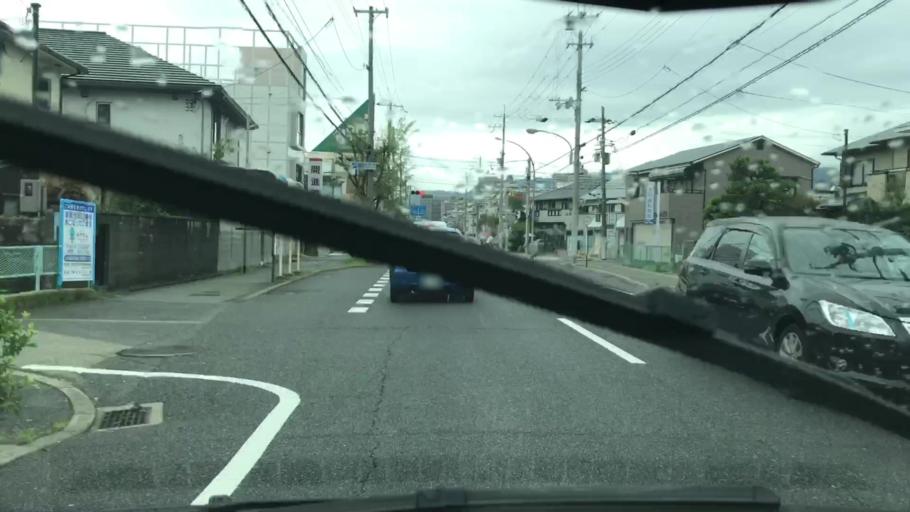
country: JP
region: Hyogo
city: Nishinomiya-hama
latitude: 34.7425
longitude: 135.3679
